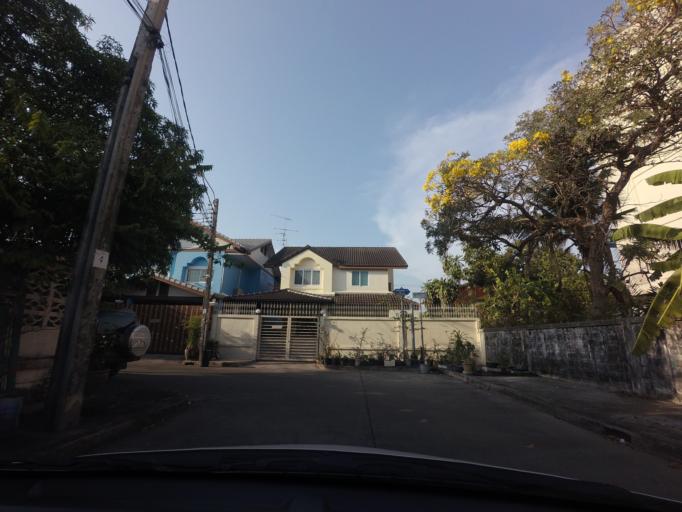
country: TH
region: Bangkok
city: Saphan Sung
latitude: 13.7437
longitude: 100.6938
